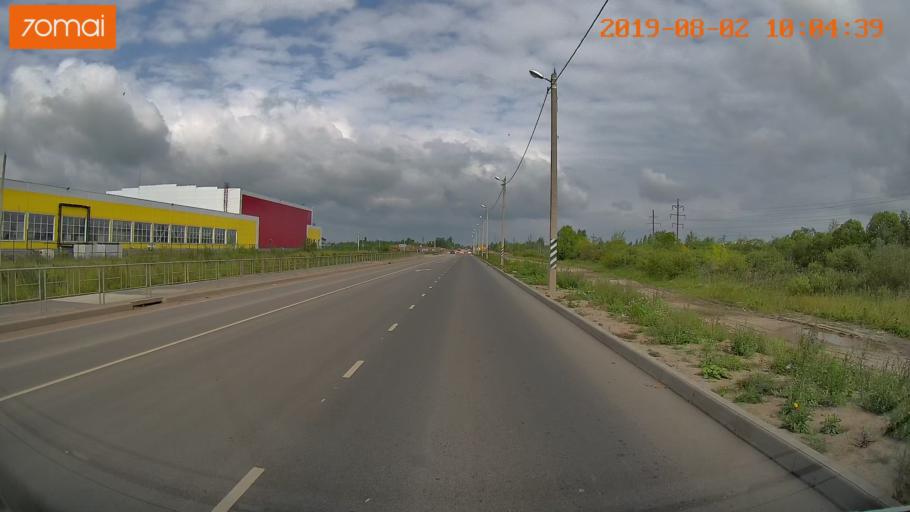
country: RU
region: Ivanovo
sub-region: Gorod Ivanovo
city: Ivanovo
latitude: 56.9742
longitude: 40.9239
